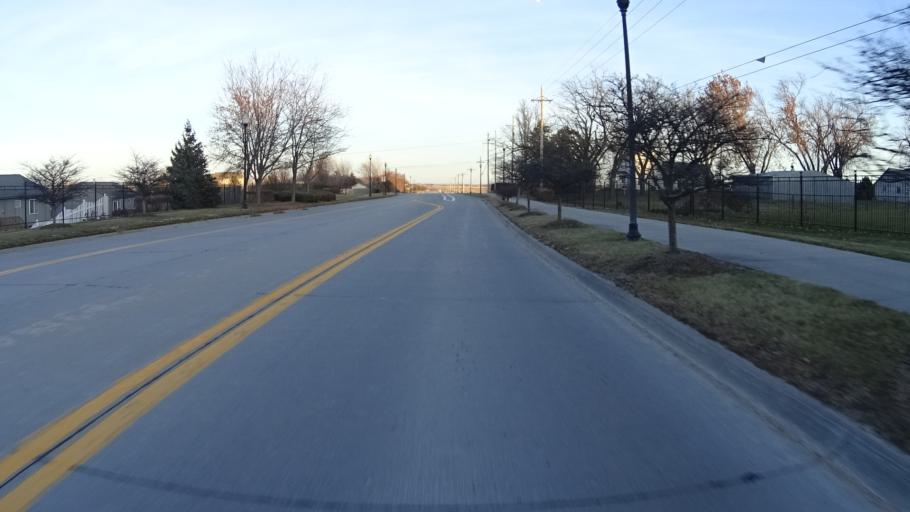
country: US
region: Nebraska
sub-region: Sarpy County
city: Papillion
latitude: 41.1326
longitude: -96.0543
